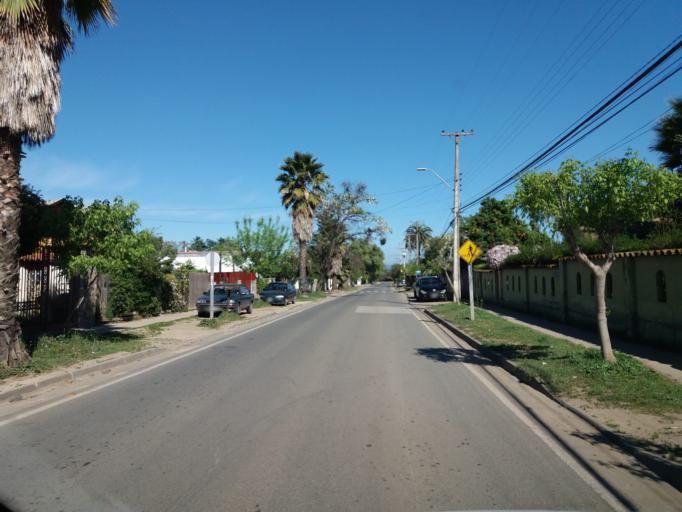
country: CL
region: Valparaiso
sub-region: Provincia de Marga Marga
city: Limache
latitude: -32.9943
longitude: -71.1731
